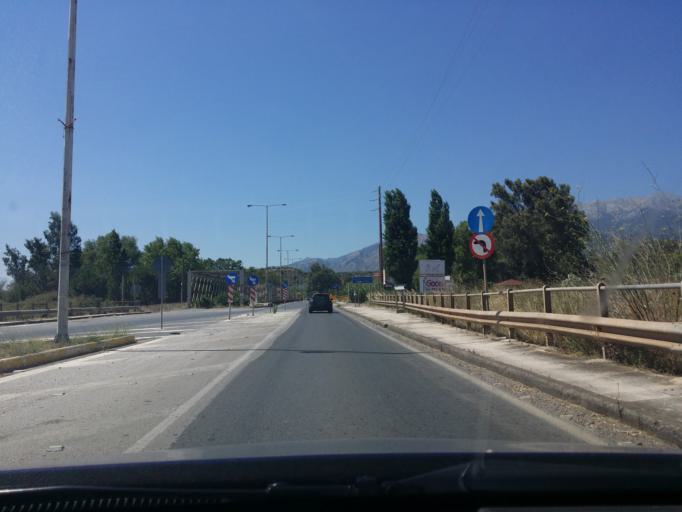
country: GR
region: Peloponnese
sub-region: Nomos Lakonias
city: Sparti
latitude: 37.0900
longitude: 22.4309
